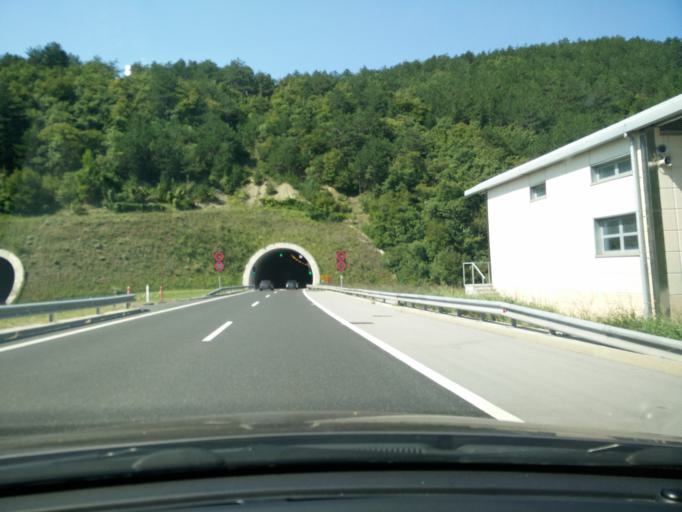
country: SI
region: Koper-Capodistria
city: Dekani
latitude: 45.5518
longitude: 13.8315
